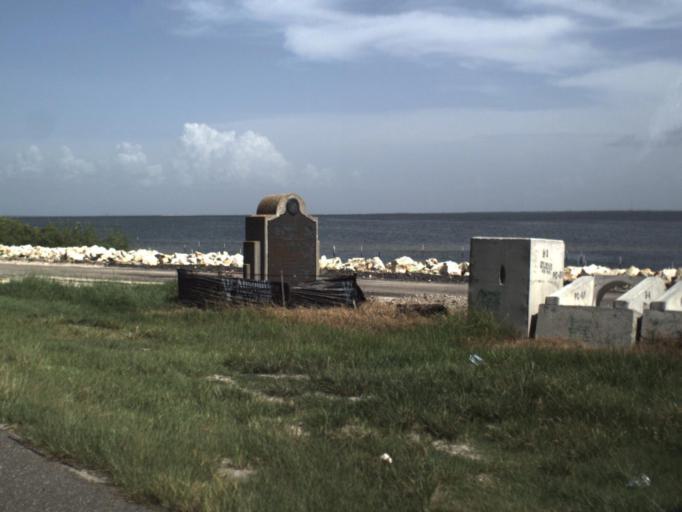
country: US
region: Florida
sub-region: Pinellas County
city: Safety Harbor
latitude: 27.9606
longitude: -82.7041
